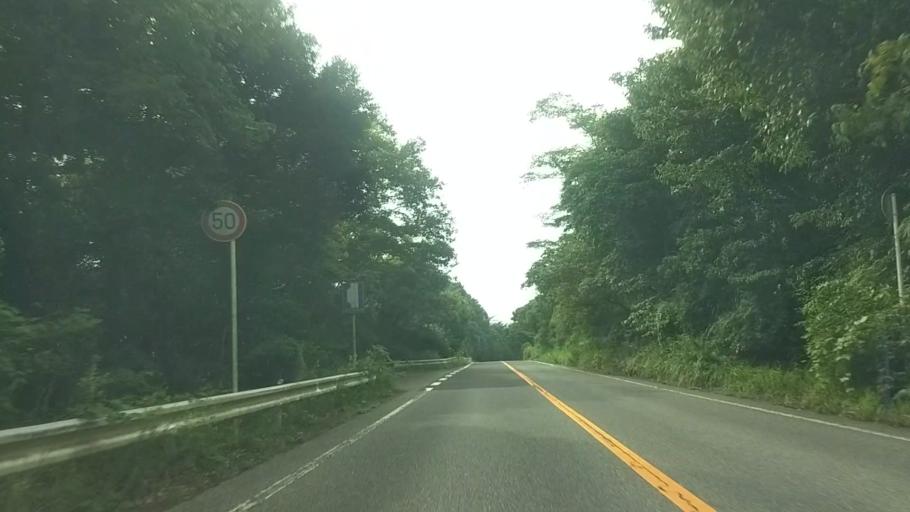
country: JP
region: Chiba
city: Kimitsu
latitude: 35.2341
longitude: 140.0111
